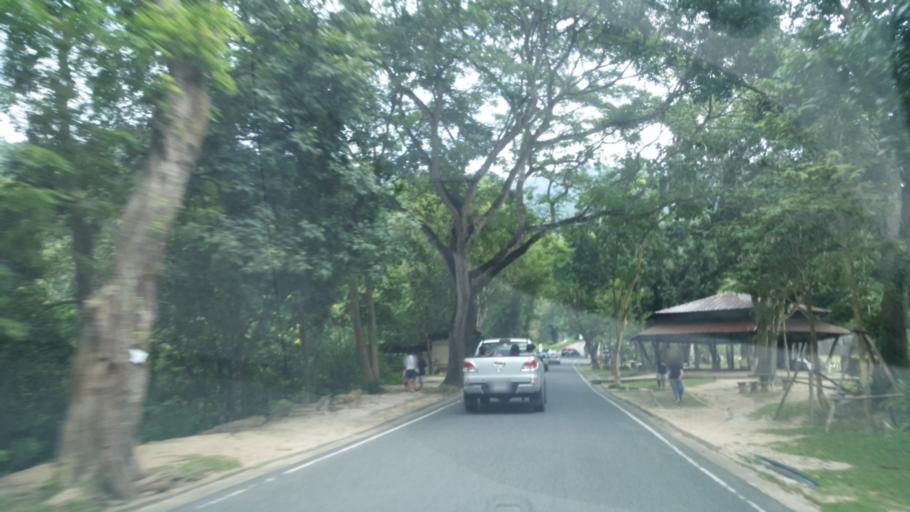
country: TH
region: Chon Buri
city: Ban Bueng
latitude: 13.2184
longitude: 101.0544
